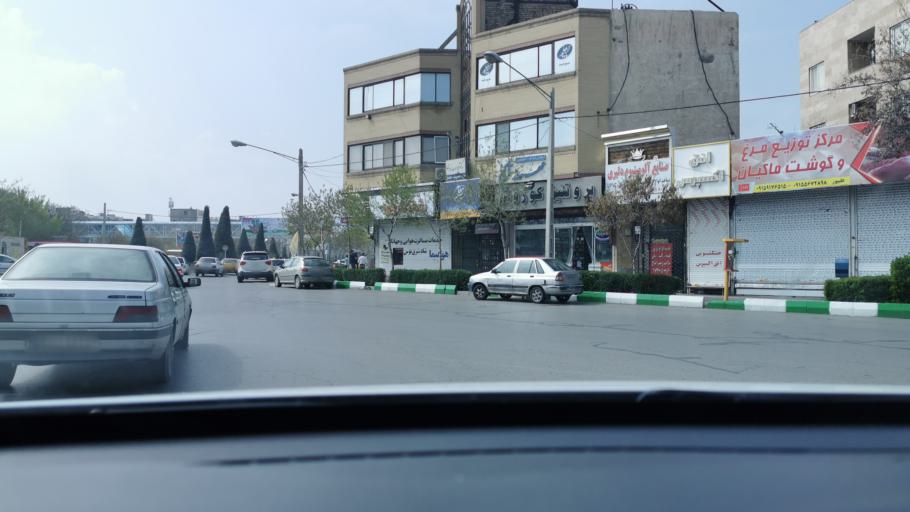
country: IR
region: Razavi Khorasan
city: Mashhad
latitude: 36.3291
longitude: 59.5287
